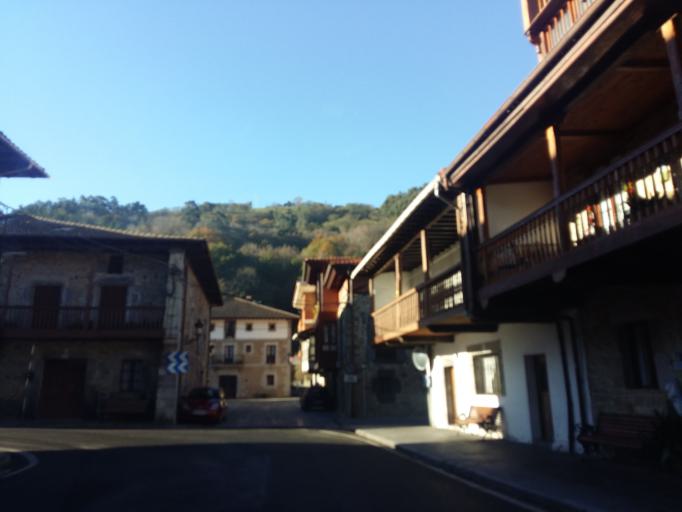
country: ES
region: Basque Country
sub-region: Bizkaia
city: Lanestosa
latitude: 43.2189
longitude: -3.4396
